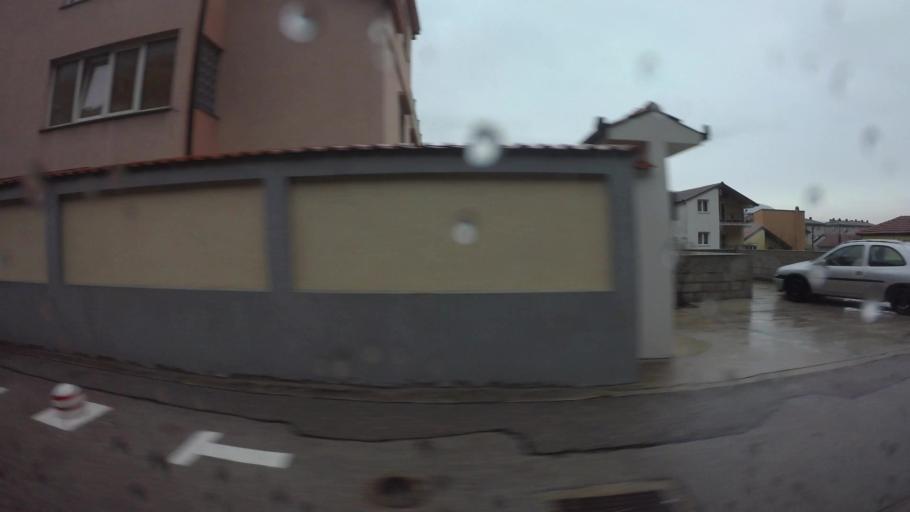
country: BA
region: Federation of Bosnia and Herzegovina
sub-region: Hercegovacko-Bosanski Kanton
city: Mostar
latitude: 43.3303
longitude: 17.8154
